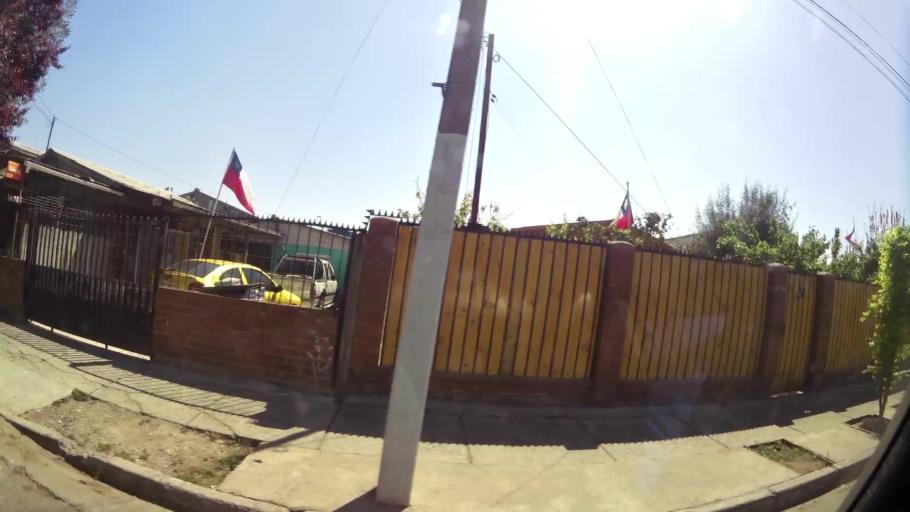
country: CL
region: Santiago Metropolitan
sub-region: Provincia de Talagante
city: Penaflor
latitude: -33.5682
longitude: -70.8110
